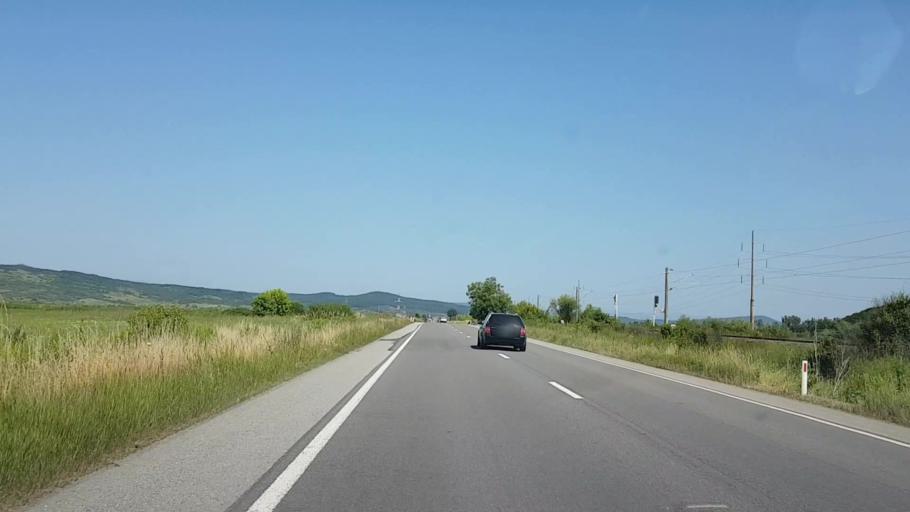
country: RO
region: Bistrita-Nasaud
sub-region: Comuna Sintereag
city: Cociu
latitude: 47.1823
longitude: 24.2428
